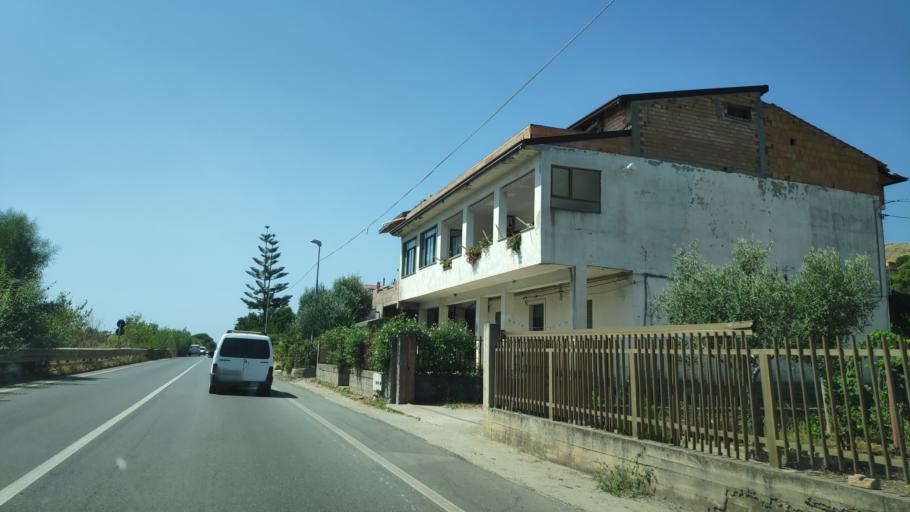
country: IT
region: Calabria
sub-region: Provincia di Reggio Calabria
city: Brancaleone-Marina
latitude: 37.9805
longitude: 16.1142
